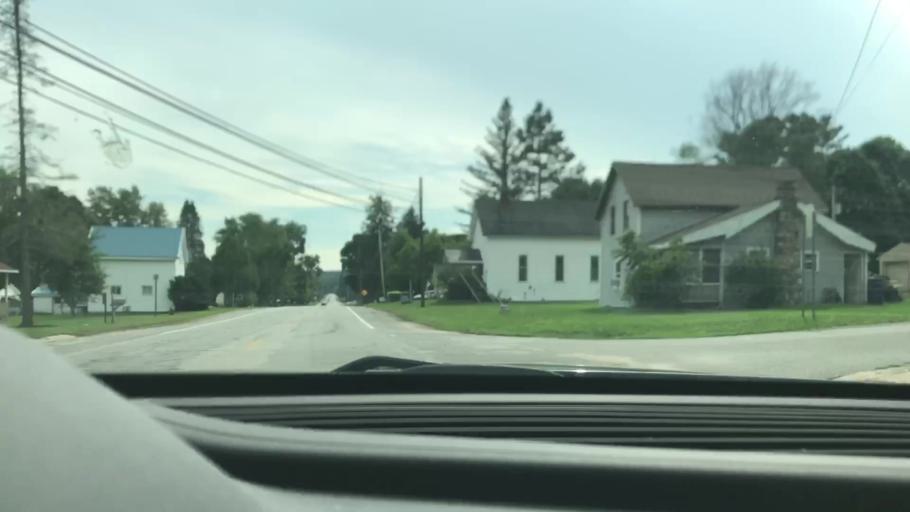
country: US
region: Michigan
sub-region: Antrim County
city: Bellaire
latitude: 45.0662
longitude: -85.2641
